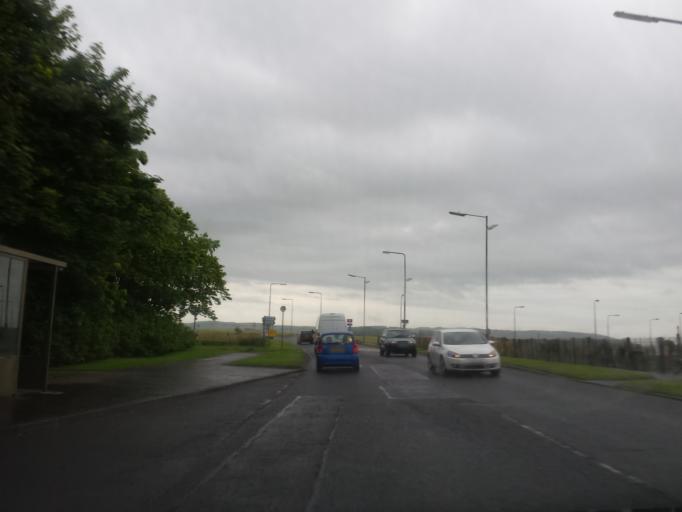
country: GB
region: Scotland
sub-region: Fife
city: Leuchars
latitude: 56.3766
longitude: -2.8913
